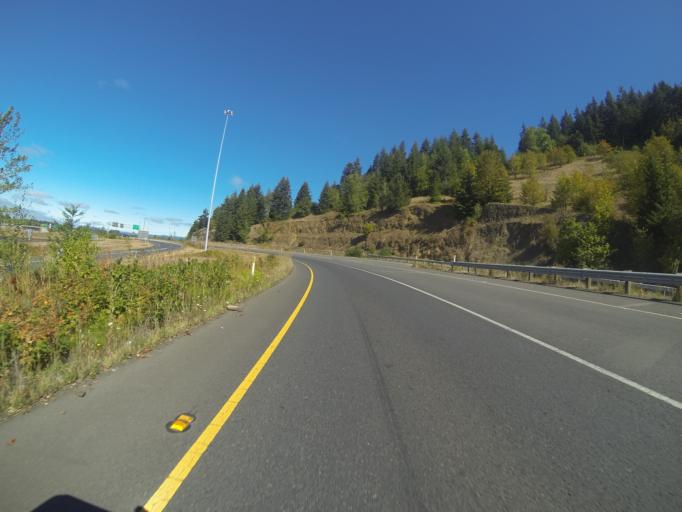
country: US
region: Washington
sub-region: Cowlitz County
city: Kelso
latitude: 46.1058
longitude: -122.8764
